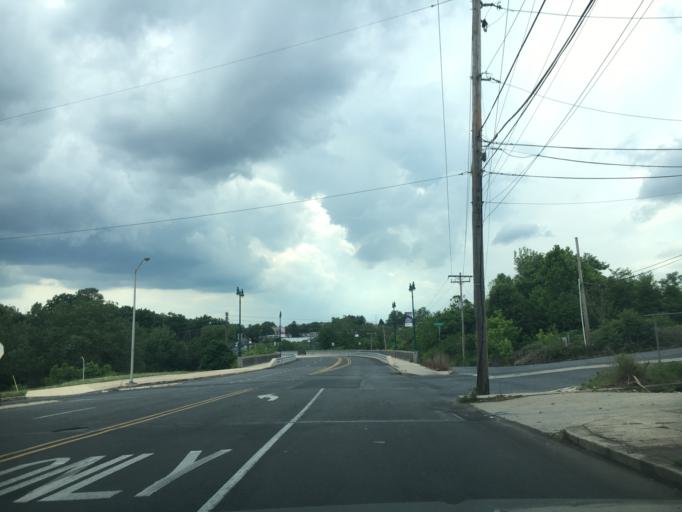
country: US
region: Pennsylvania
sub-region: Berks County
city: West Reading
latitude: 40.3404
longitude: -75.9405
